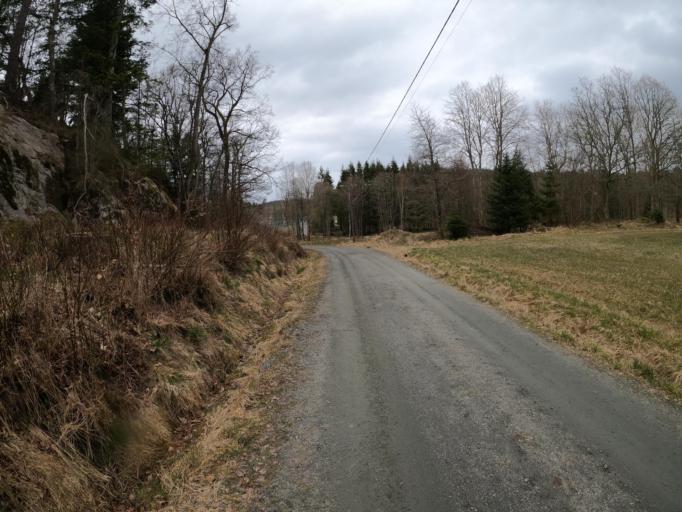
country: SE
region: Vaestra Goetaland
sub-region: Harryda Kommun
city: Molnlycke
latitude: 57.6253
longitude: 12.1075
